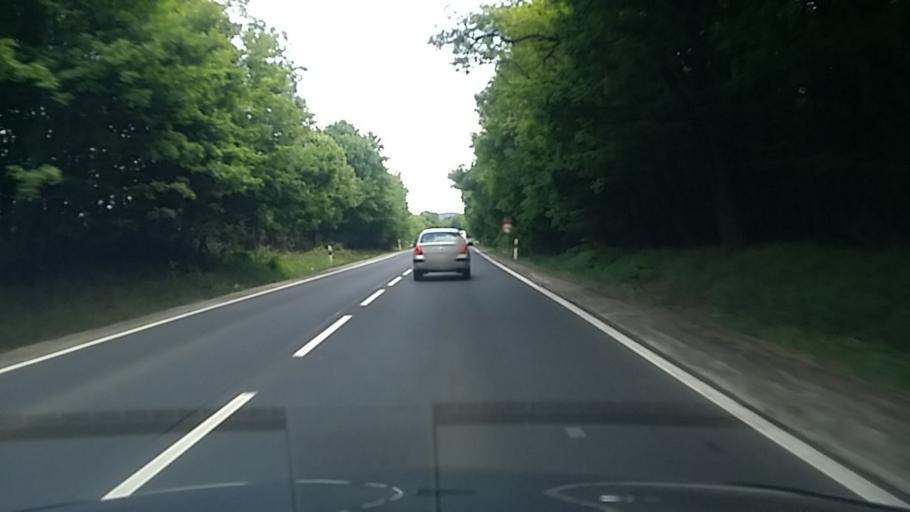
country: HU
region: Nograd
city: Retsag
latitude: 47.8782
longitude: 19.1048
